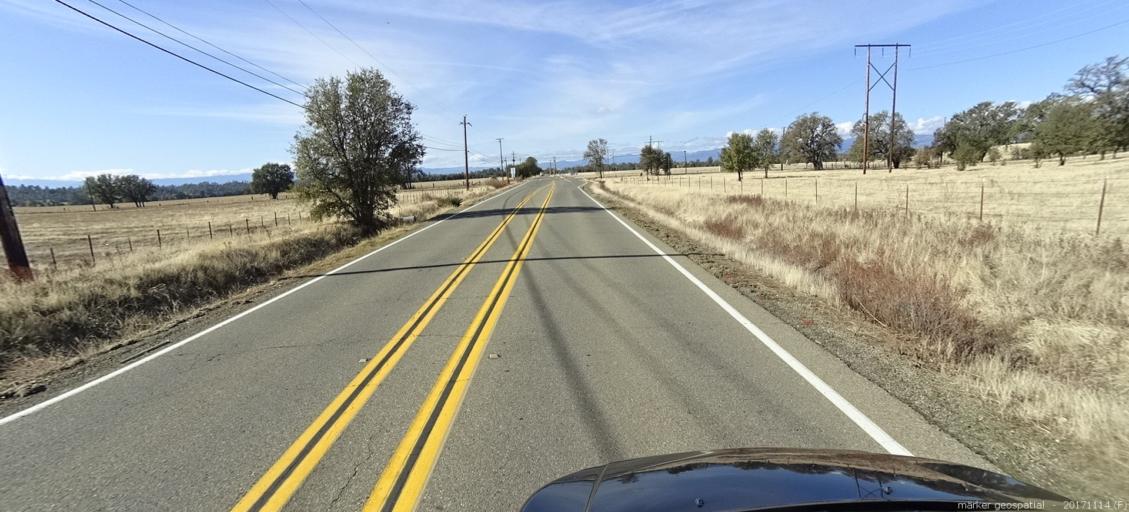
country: US
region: California
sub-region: Shasta County
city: Anderson
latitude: 40.3886
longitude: -122.4048
